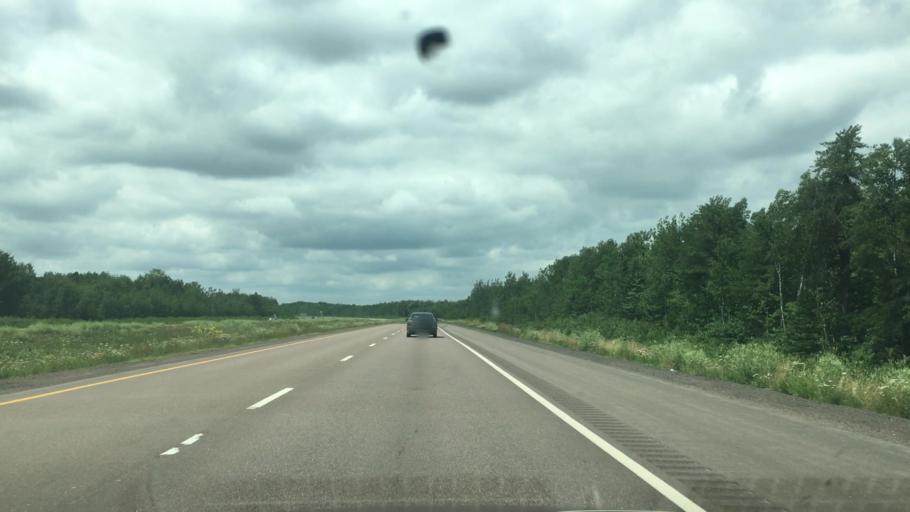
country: CA
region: New Brunswick
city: Dieppe
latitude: 46.1296
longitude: -64.6555
